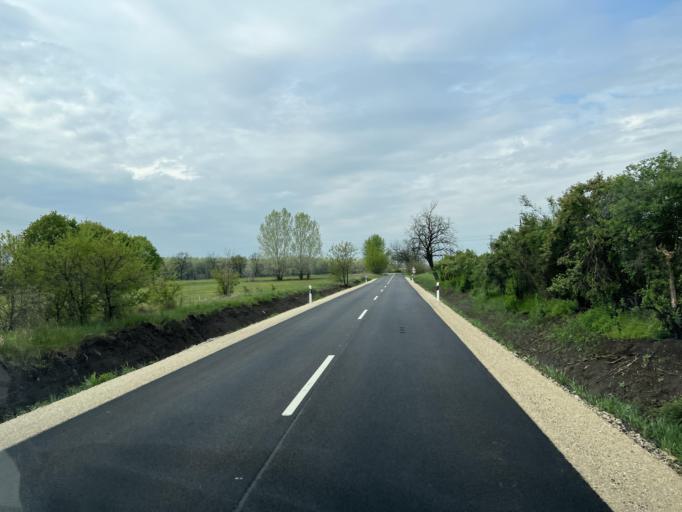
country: HU
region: Pest
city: Danszentmiklos
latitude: 47.2257
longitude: 19.5762
